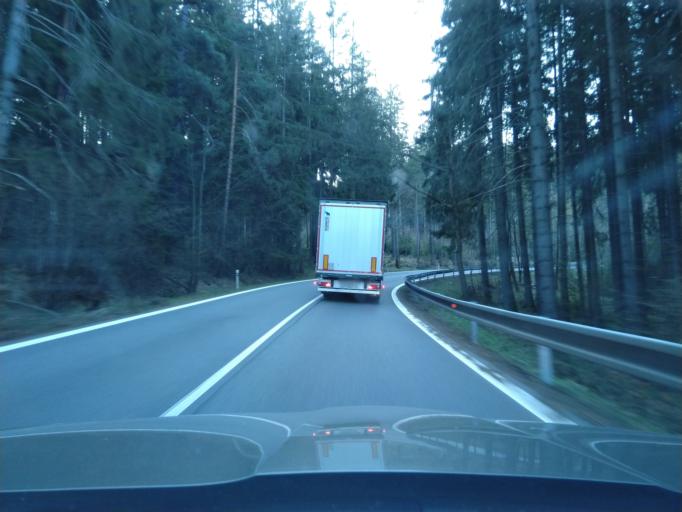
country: CZ
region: Jihocesky
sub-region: Okres Prachatice
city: Vimperk
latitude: 49.0392
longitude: 13.7629
